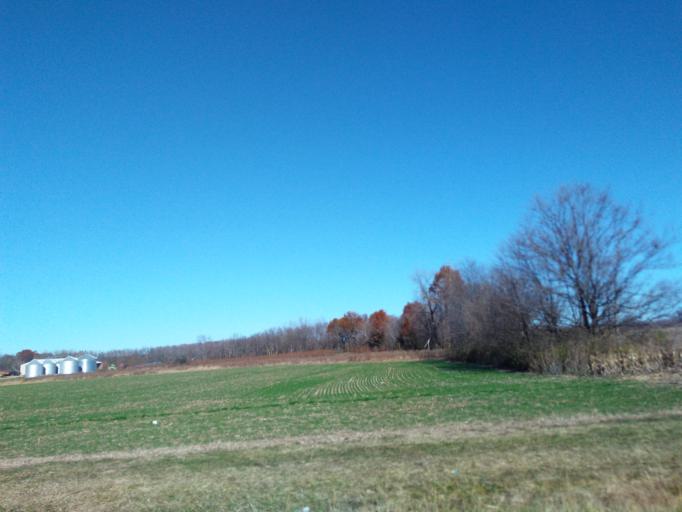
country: US
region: Illinois
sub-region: Madison County
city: Saint Jacob
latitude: 38.7165
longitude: -89.7959
